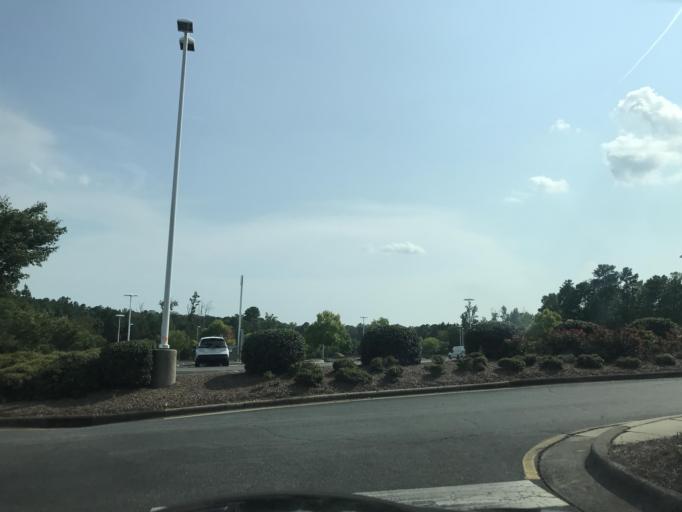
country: US
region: North Carolina
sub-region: Wake County
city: Morrisville
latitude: 35.8568
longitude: -78.8868
